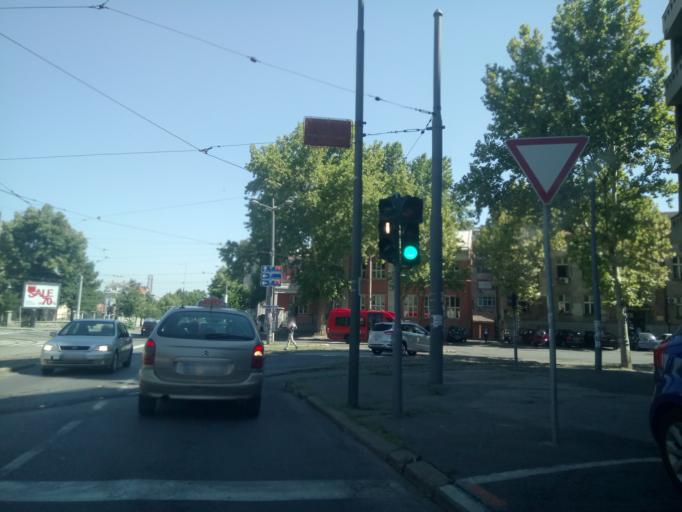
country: RS
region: Central Serbia
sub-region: Belgrade
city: Stari Grad
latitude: 44.8253
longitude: 20.4557
